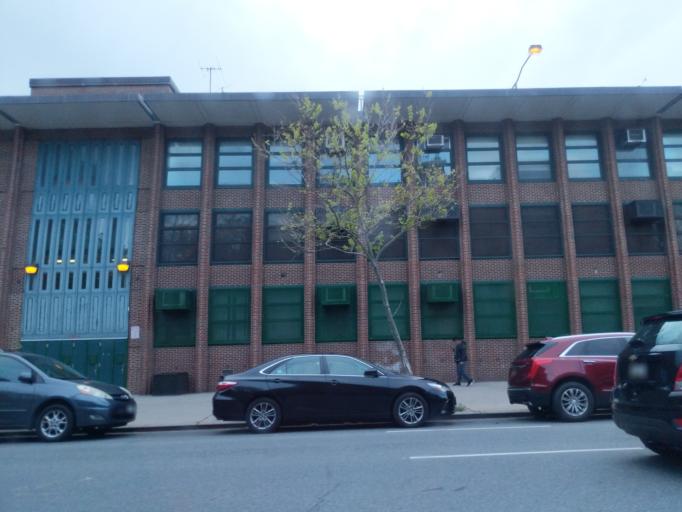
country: US
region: New York
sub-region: New York County
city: Manhattan
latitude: 40.7969
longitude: -73.9408
